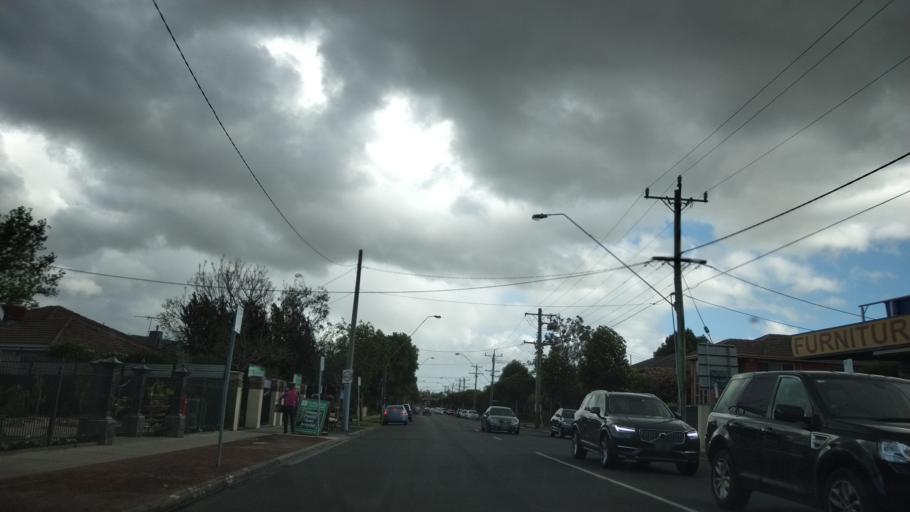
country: AU
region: Victoria
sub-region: Glen Eira
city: Glen Huntly
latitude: -37.8899
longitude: 145.0449
